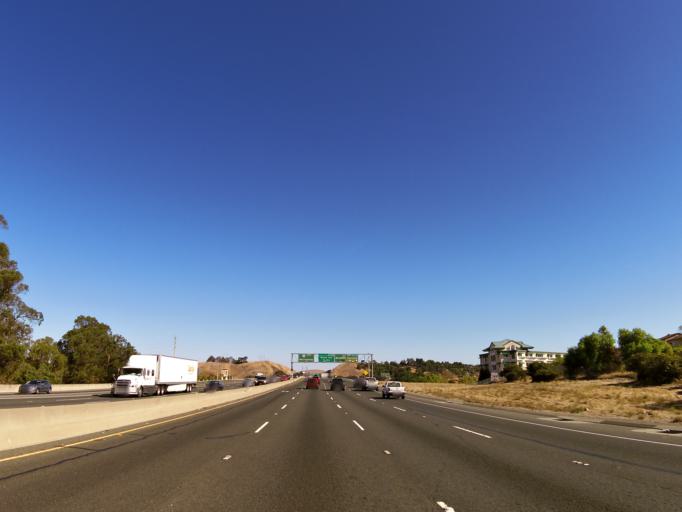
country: US
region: California
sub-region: Contra Costa County
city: Hercules
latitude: 38.0086
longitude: -122.2752
